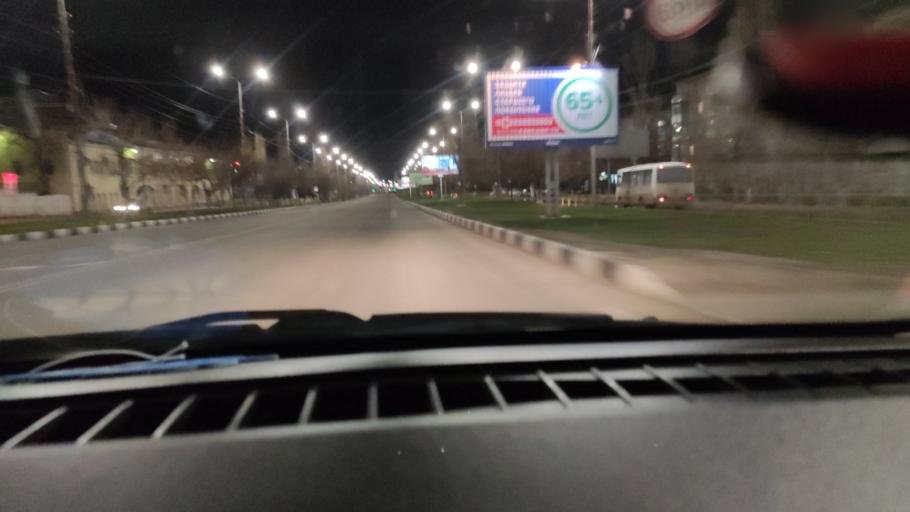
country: RU
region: Saratov
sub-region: Saratovskiy Rayon
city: Saratov
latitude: 51.6039
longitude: 45.9690
